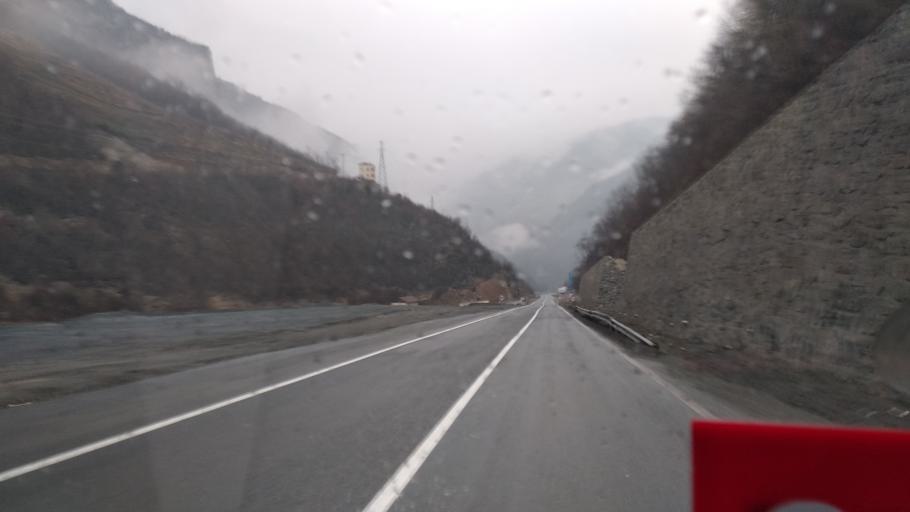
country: TR
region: Trabzon
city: Macka
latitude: 40.7401
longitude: 39.5496
